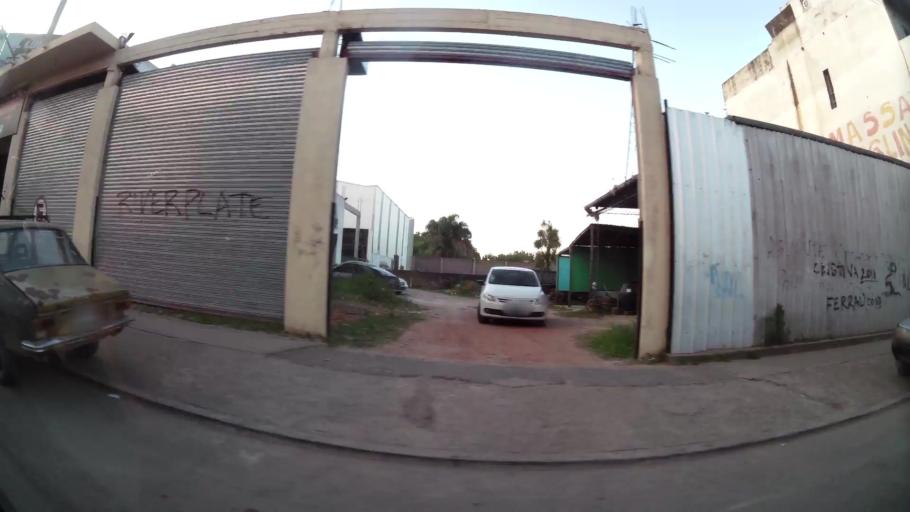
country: AR
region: Buenos Aires
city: Santa Catalina - Dique Lujan
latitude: -34.4688
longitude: -58.7555
